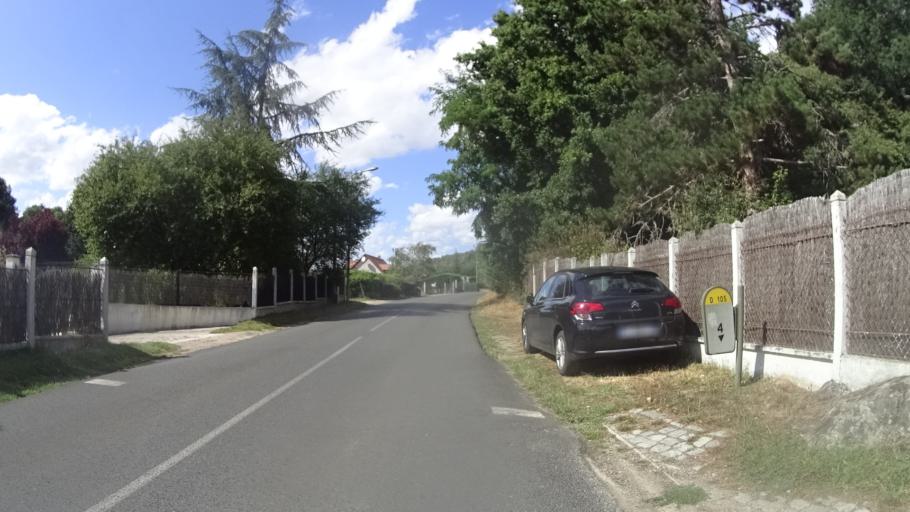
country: FR
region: Ile-de-France
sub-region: Departement de l'Essonne
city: Boutigny-sur-Essonne
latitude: 48.4499
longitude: 2.3665
